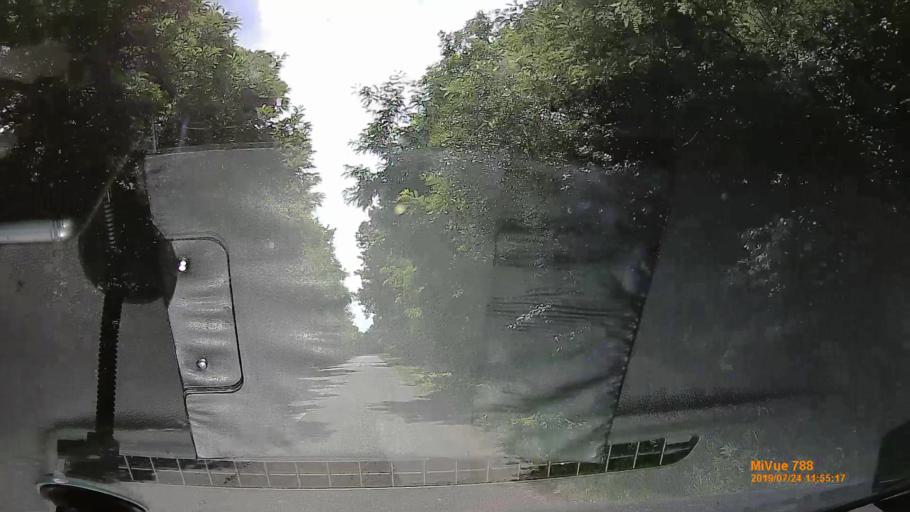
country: HU
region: Szabolcs-Szatmar-Bereg
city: Vasarosnameny
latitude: 48.2105
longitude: 22.4136
